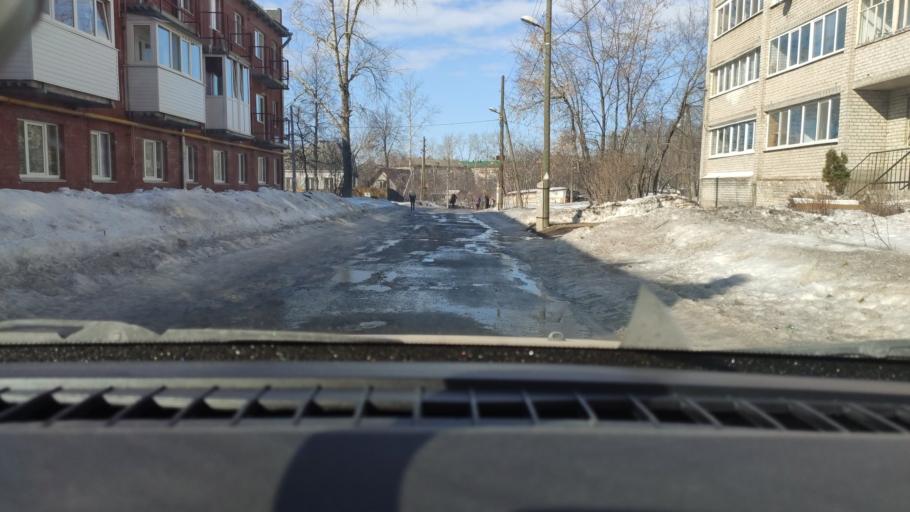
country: RU
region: Perm
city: Polazna
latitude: 58.1277
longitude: 56.3843
